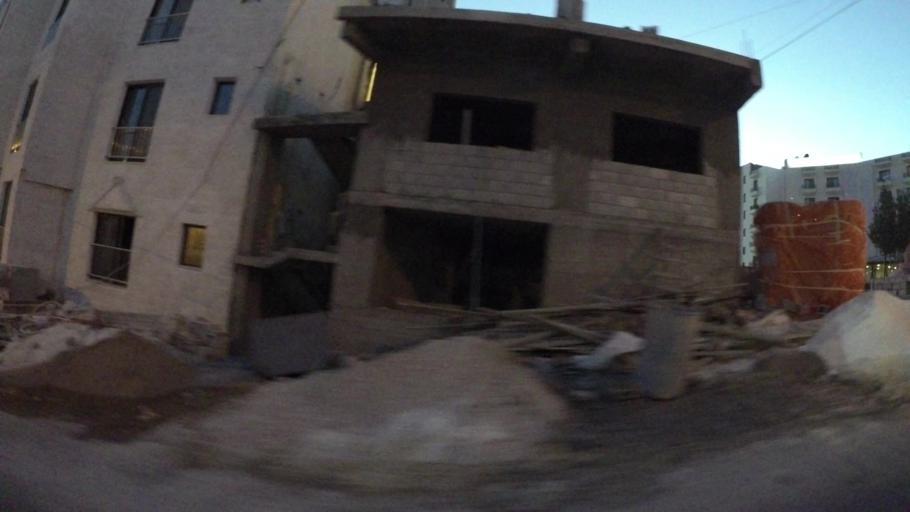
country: JO
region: Ma'an
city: Petra
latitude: 30.3255
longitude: 35.4714
